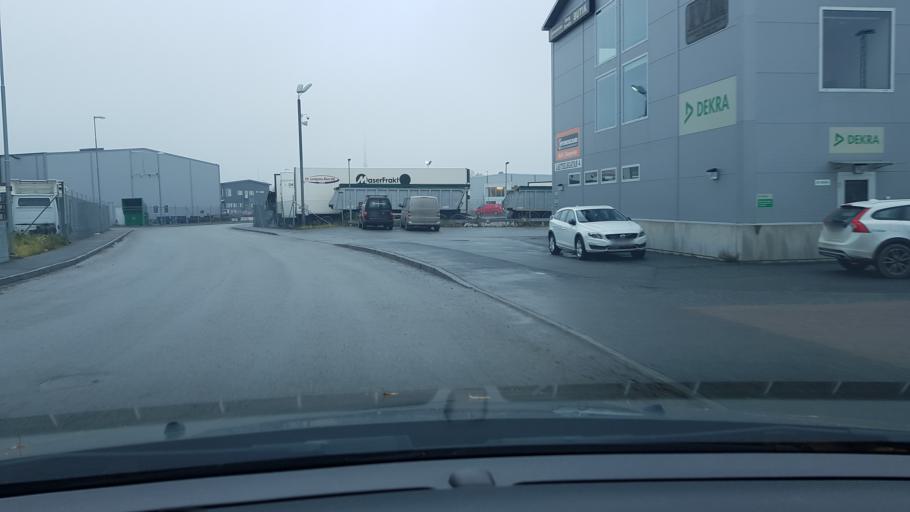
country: SE
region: Uppsala
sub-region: Uppsala Kommun
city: Saevja
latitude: 59.8434
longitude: 17.7258
